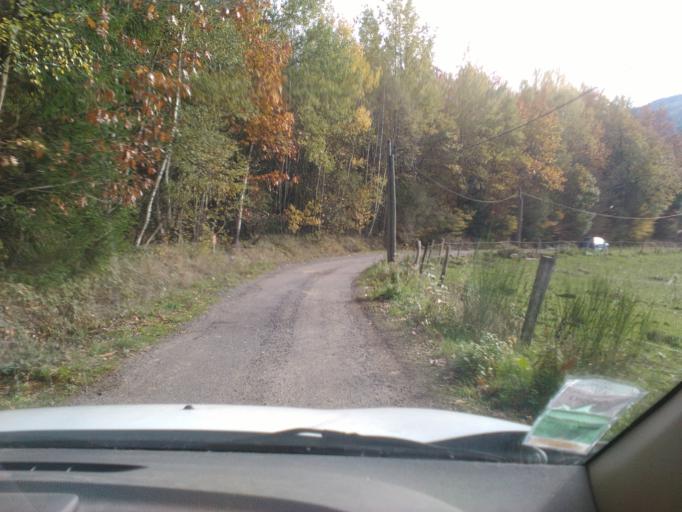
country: FR
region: Lorraine
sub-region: Departement des Vosges
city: Moyenmoutier
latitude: 48.4196
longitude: 6.8752
